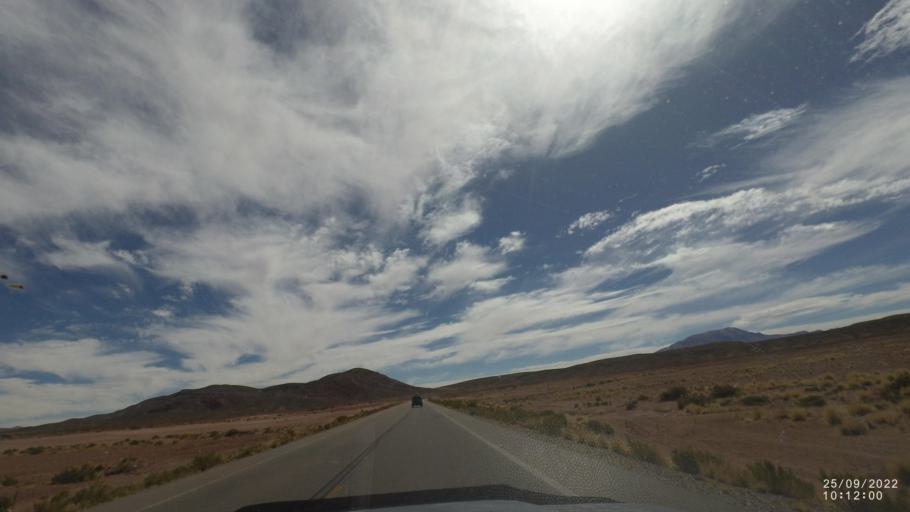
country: BO
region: Potosi
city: Colchani
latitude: -20.0923
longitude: -66.8987
